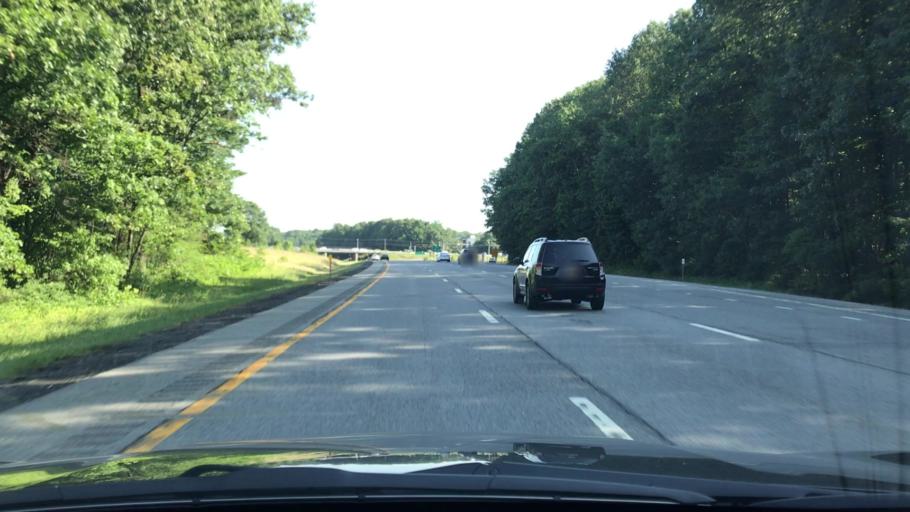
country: US
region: New York
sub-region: Saratoga County
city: Saratoga Springs
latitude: 43.1007
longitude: -73.7534
